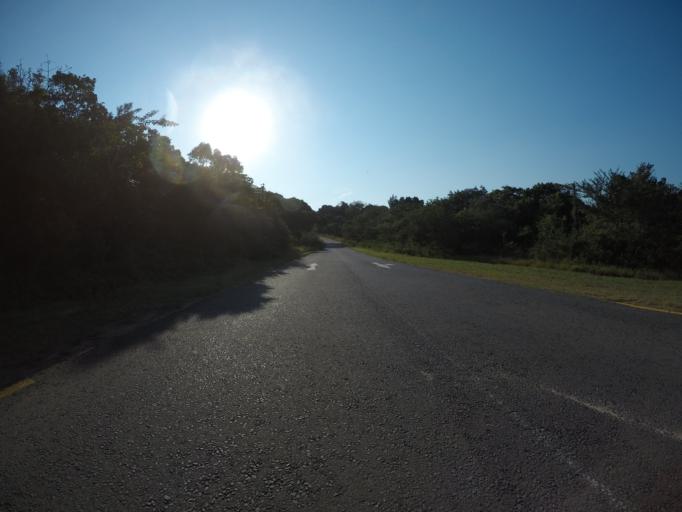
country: ZA
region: KwaZulu-Natal
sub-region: uThungulu District Municipality
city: Richards Bay
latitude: -28.7829
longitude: 32.0856
